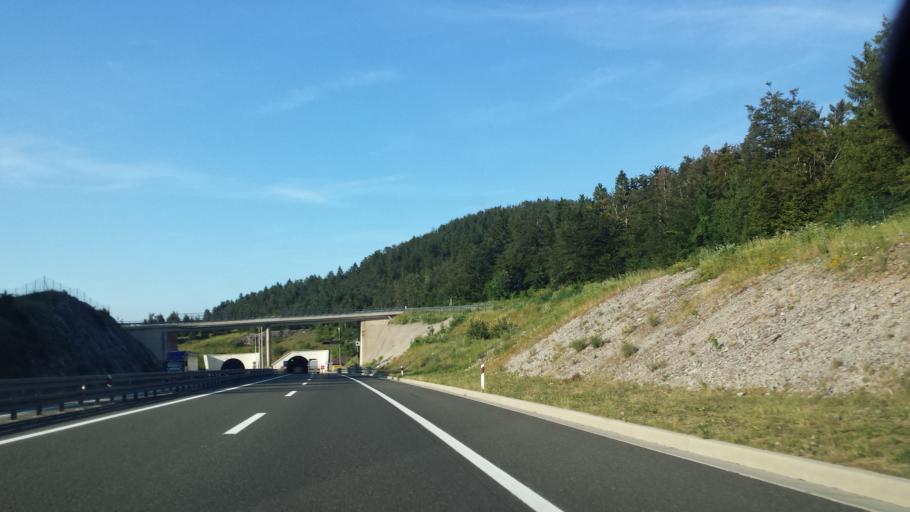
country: HR
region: Primorsko-Goranska
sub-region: Grad Delnice
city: Delnice
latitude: 45.3618
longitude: 14.7668
